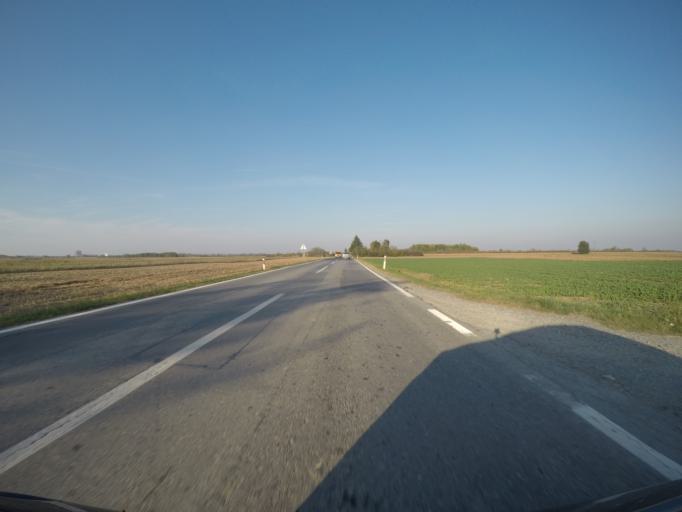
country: HU
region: Somogy
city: Barcs
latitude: 45.9211
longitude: 17.4520
